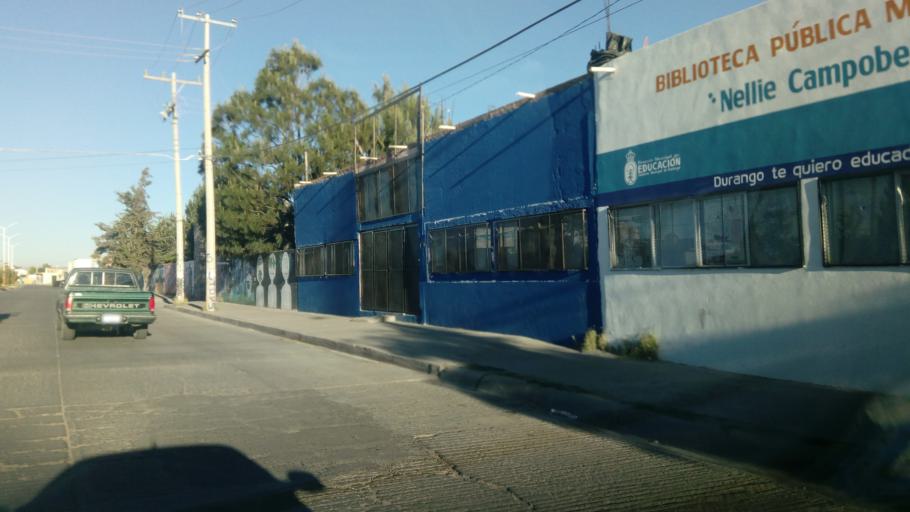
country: MX
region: Durango
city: Victoria de Durango
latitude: 24.0560
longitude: -104.5915
